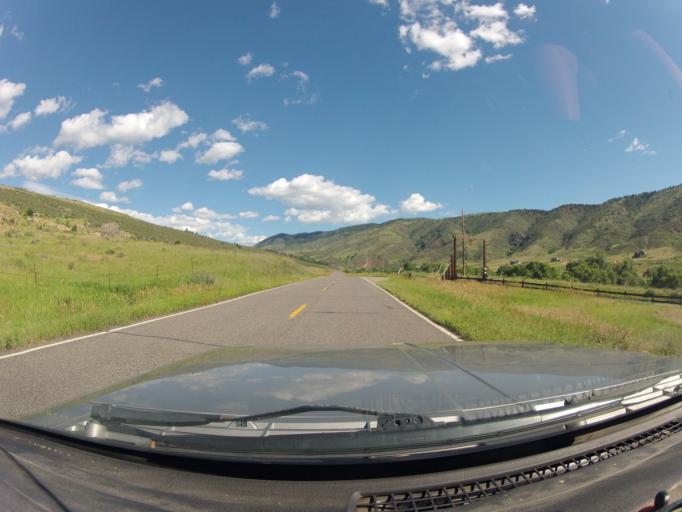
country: US
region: Colorado
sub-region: Larimer County
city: Laporte
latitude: 40.4995
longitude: -105.2251
